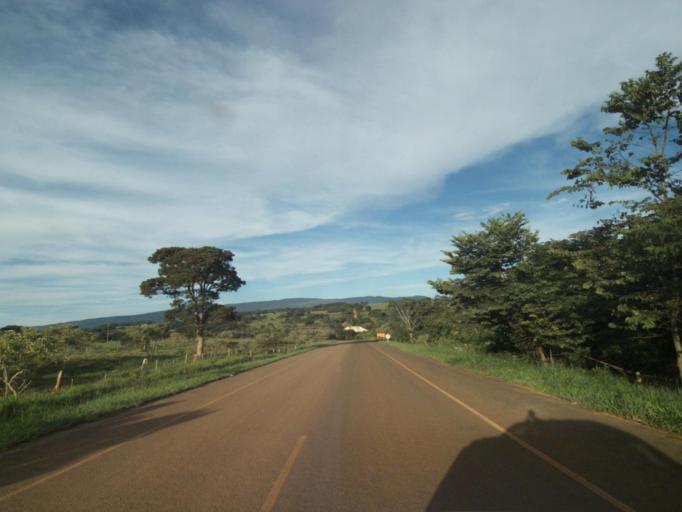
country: BR
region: Goias
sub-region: Jaragua
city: Jaragua
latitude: -15.8606
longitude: -49.3930
